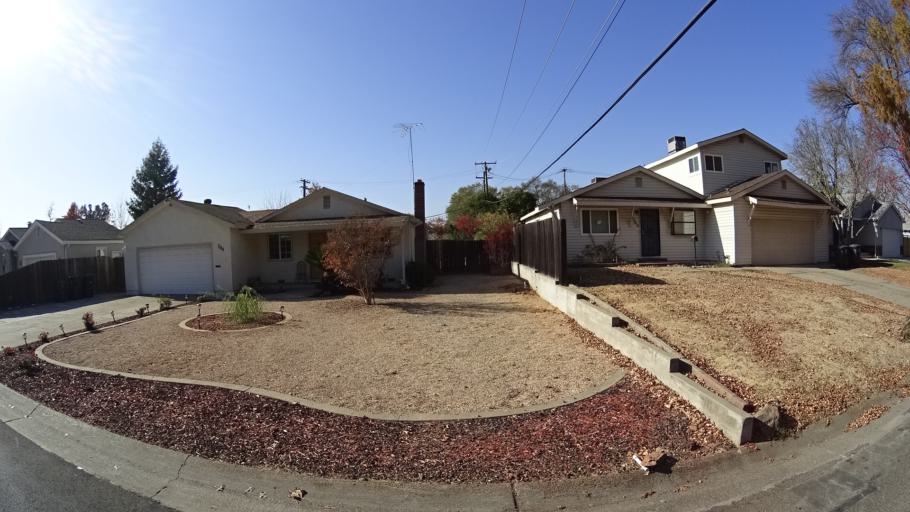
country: US
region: California
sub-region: Sacramento County
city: Citrus Heights
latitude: 38.6856
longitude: -121.2870
